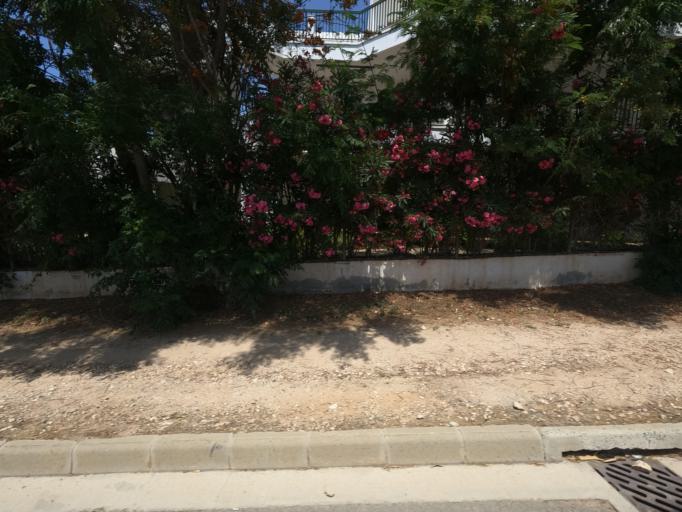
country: CY
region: Ammochostos
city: Ayia Napa
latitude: 34.9840
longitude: 34.0170
